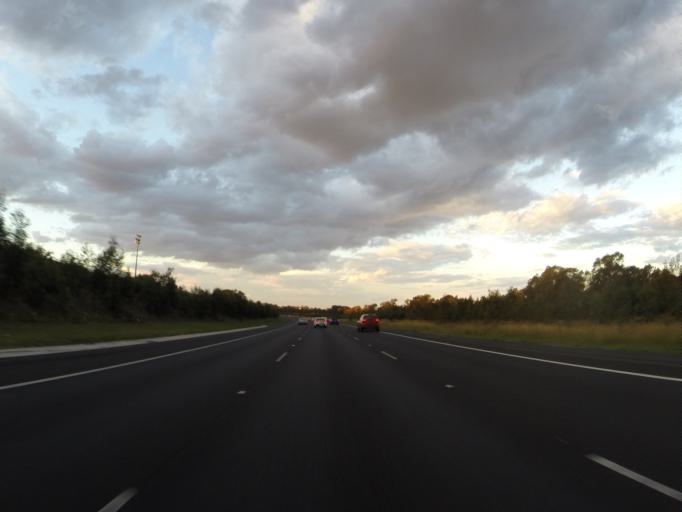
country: AU
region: New South Wales
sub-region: Campbelltown Municipality
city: Leumeah
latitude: -34.0451
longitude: 150.8193
